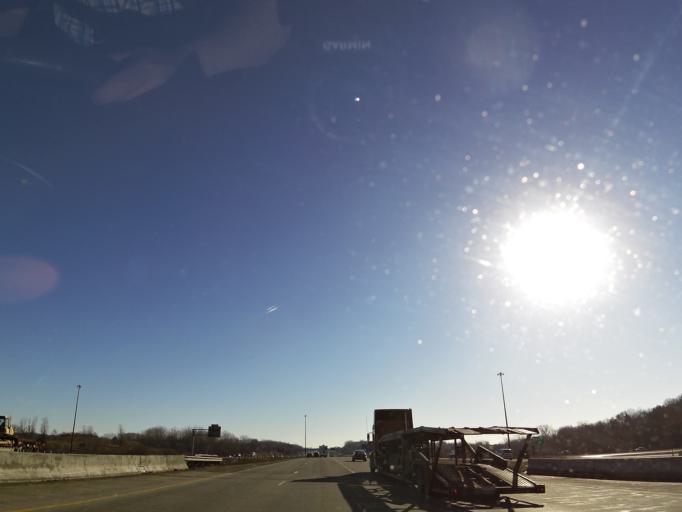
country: US
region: Minnesota
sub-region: Dakota County
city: Mendota Heights
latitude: 44.8627
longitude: -93.1449
